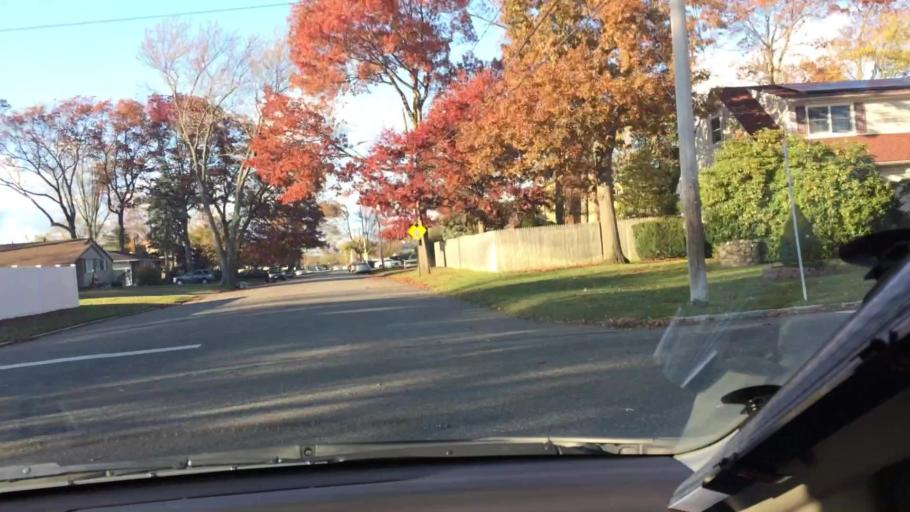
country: US
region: New York
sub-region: Suffolk County
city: Deer Park
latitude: 40.7493
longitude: -73.3342
